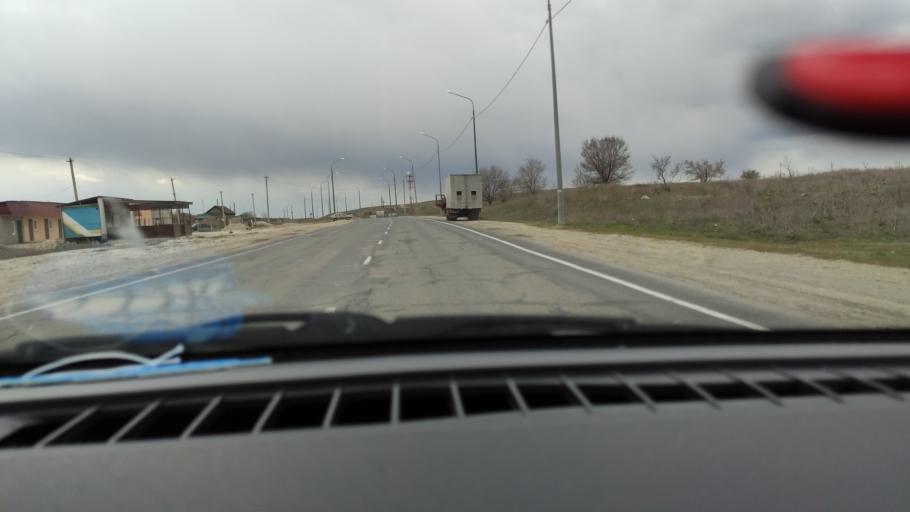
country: RU
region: Saratov
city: Sinodskoye
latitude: 52.0858
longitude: 46.8019
